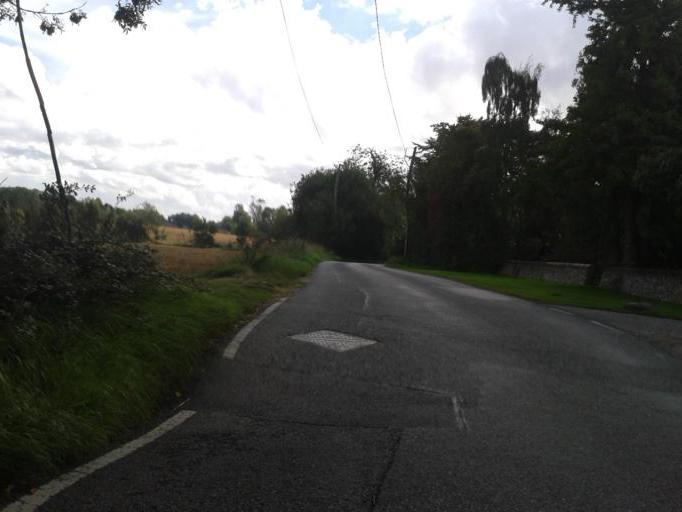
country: GB
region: England
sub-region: Cambridgeshire
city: Duxford
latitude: 52.0091
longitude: 0.1237
